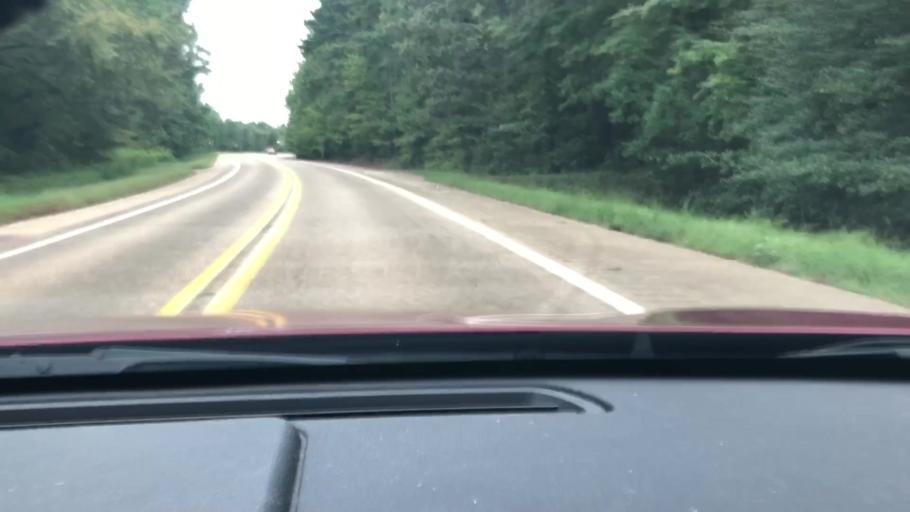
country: US
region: Arkansas
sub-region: Miller County
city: Texarkana
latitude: 33.4195
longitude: -93.8228
